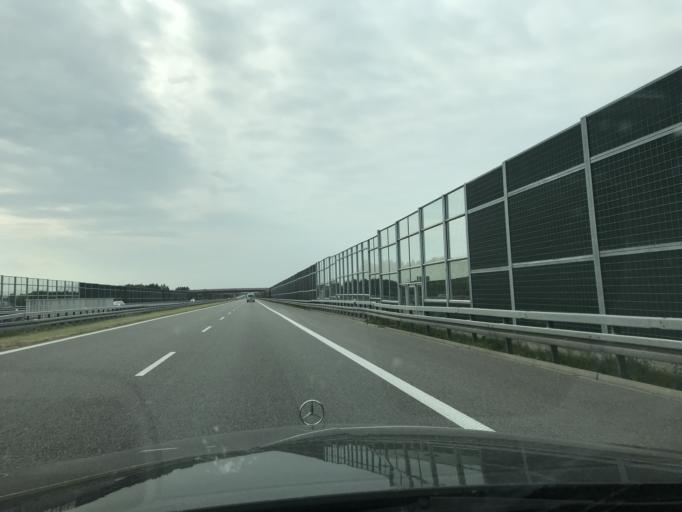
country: PL
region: Subcarpathian Voivodeship
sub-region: Powiat ropczycko-sedziszowski
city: Ostrow
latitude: 50.1048
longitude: 21.5751
